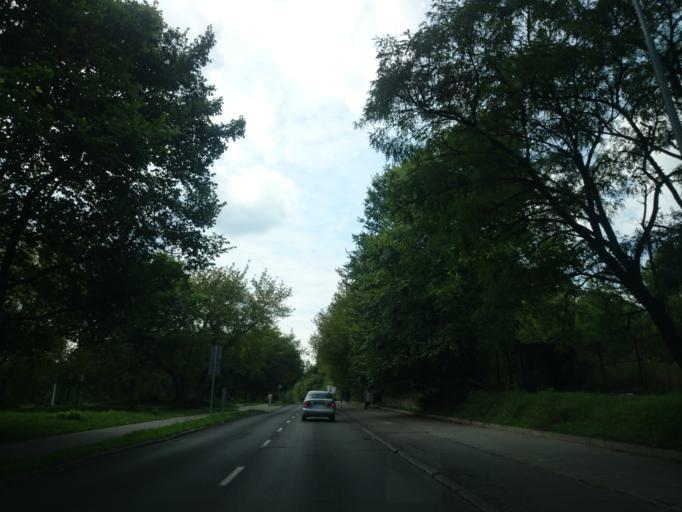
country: PL
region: West Pomeranian Voivodeship
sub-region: Szczecin
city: Szczecin
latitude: 53.4345
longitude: 14.5219
